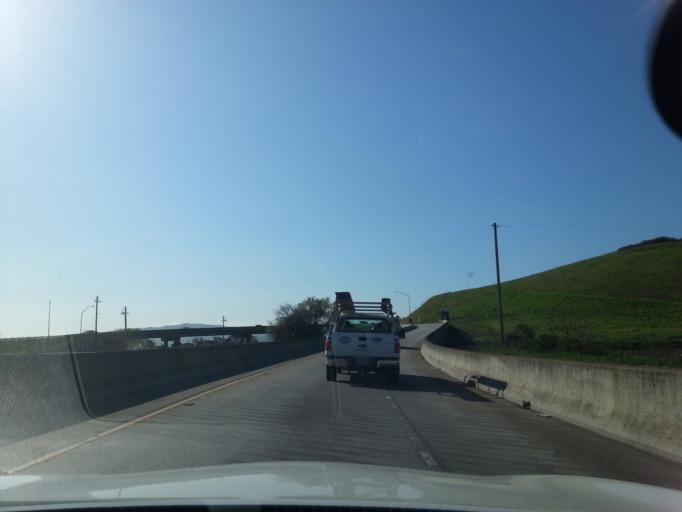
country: US
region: California
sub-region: Santa Clara County
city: Gilroy
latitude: 36.9629
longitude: -121.5516
